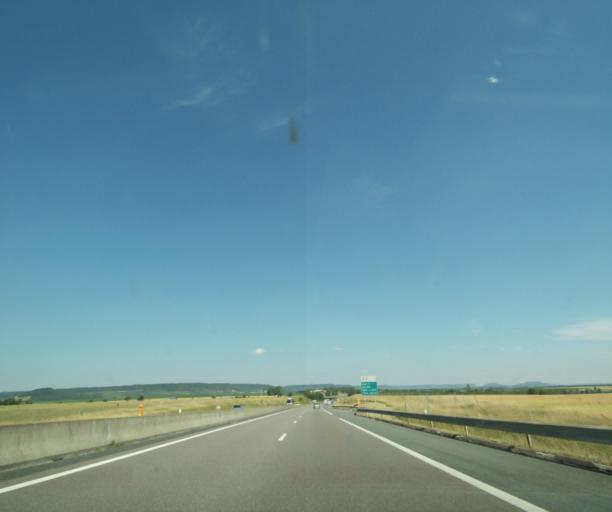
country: FR
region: Lorraine
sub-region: Departement de Meurthe-et-Moselle
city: Colombey-les-Belles
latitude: 48.5420
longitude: 5.9019
